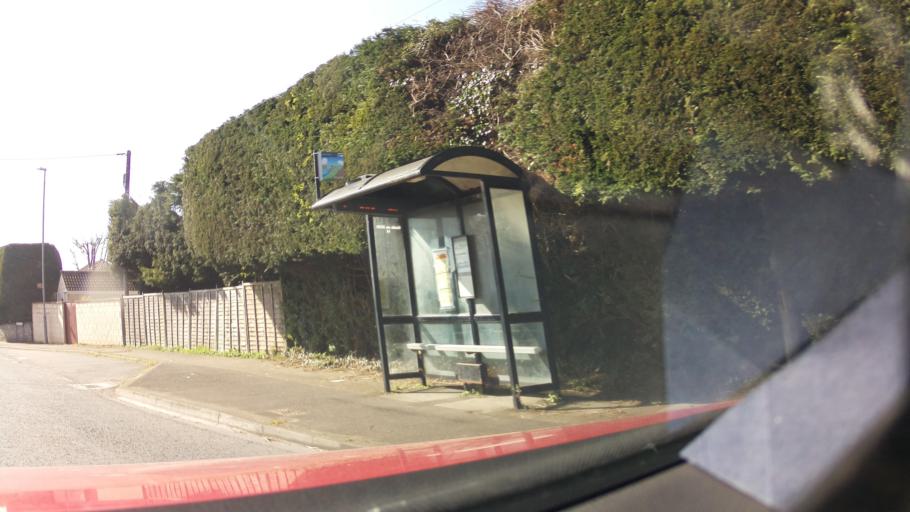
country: GB
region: England
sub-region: Wiltshire
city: Bradford-on-Avon
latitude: 51.3381
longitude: -2.2412
